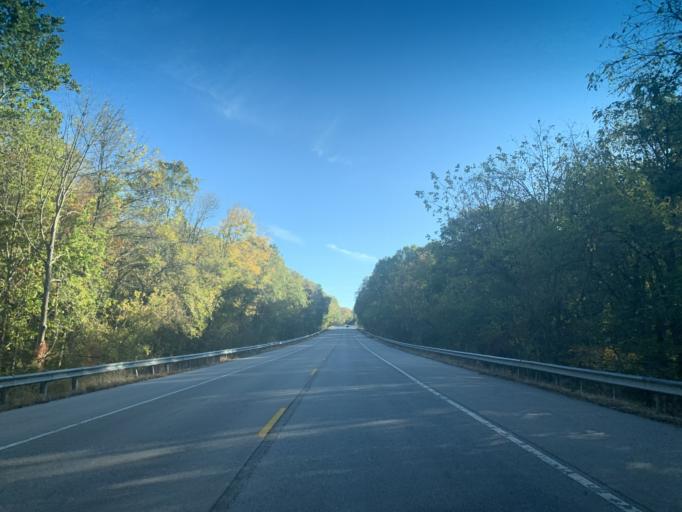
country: US
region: Maryland
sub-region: Cecil County
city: Rising Sun
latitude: 39.7107
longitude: -76.0585
